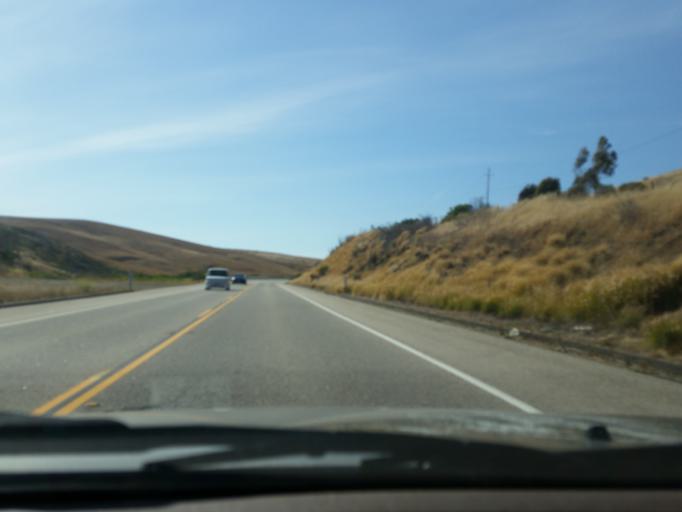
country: US
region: California
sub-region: San Luis Obispo County
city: Cayucos
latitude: 35.4790
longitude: -120.9927
